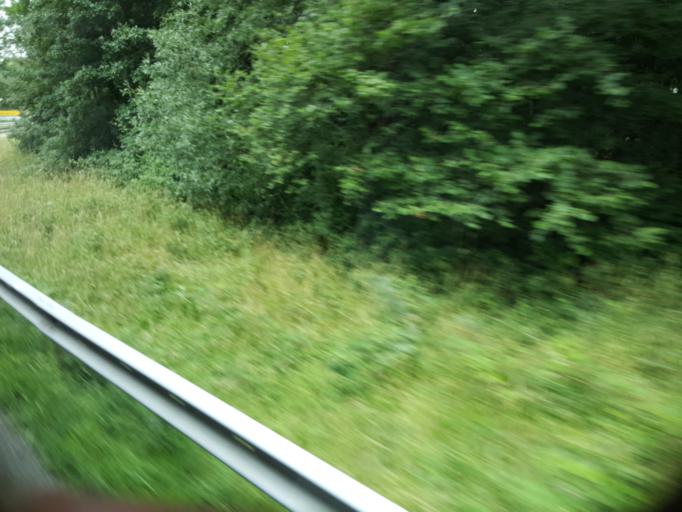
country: DE
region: North Rhine-Westphalia
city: Bad Oeynhausen
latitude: 52.2035
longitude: 8.7607
